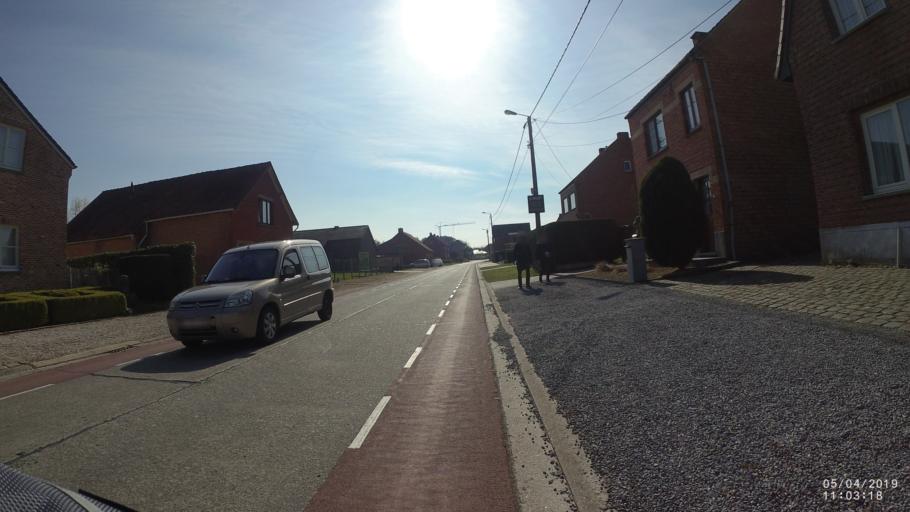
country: BE
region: Flanders
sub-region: Provincie Limburg
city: Lummen
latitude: 50.9611
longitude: 5.1884
